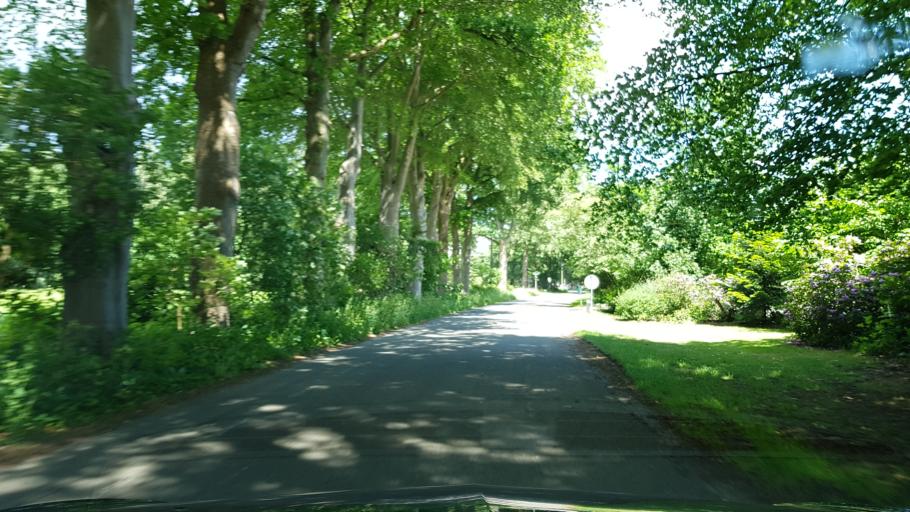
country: NL
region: Gelderland
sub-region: Gemeente Epe
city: Emst
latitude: 52.3497
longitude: 5.9176
